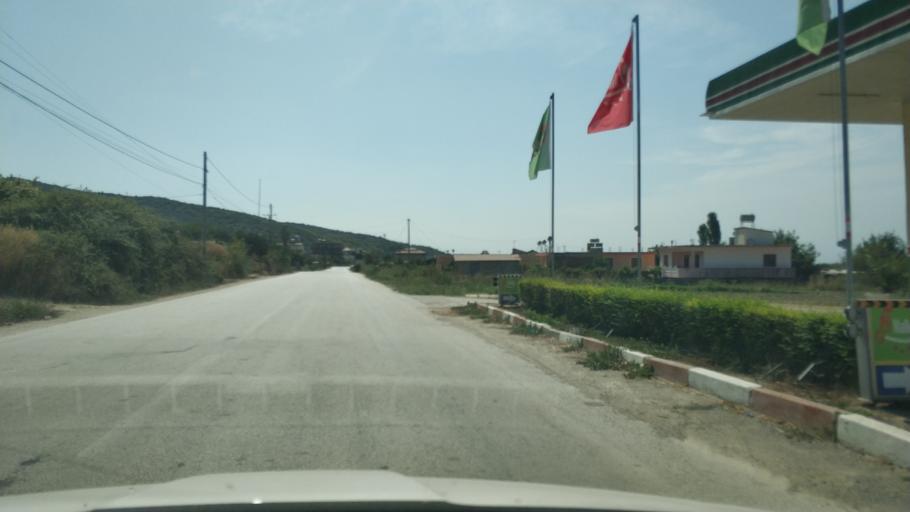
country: AL
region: Fier
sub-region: Rrethi i Lushnjes
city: Grabjan
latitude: 40.9439
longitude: 19.5373
